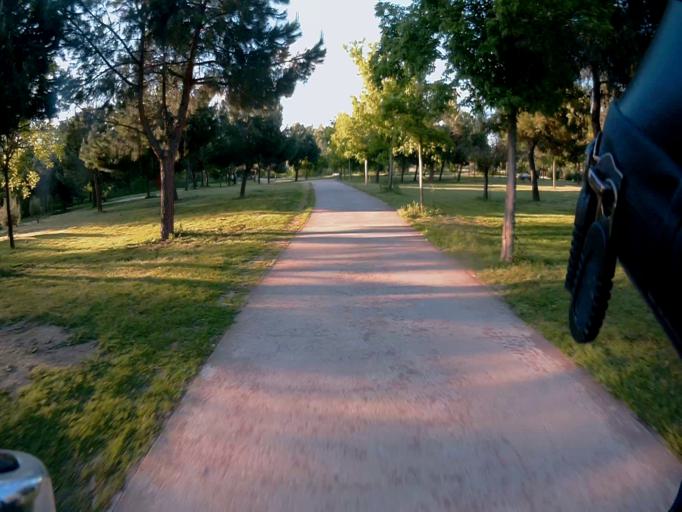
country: ES
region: Madrid
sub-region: Provincia de Madrid
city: Fuenlabrada
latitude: 40.3147
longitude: -3.7937
